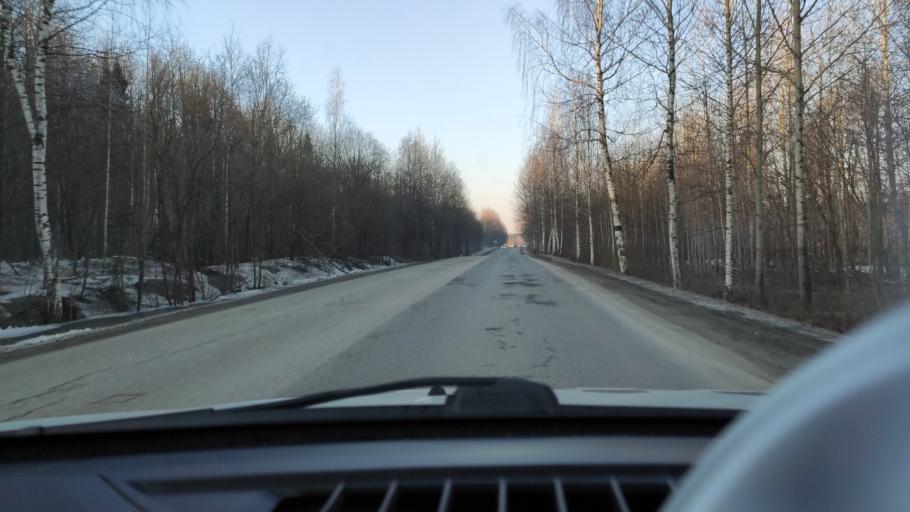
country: RU
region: Perm
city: Perm
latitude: 58.1001
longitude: 56.4099
